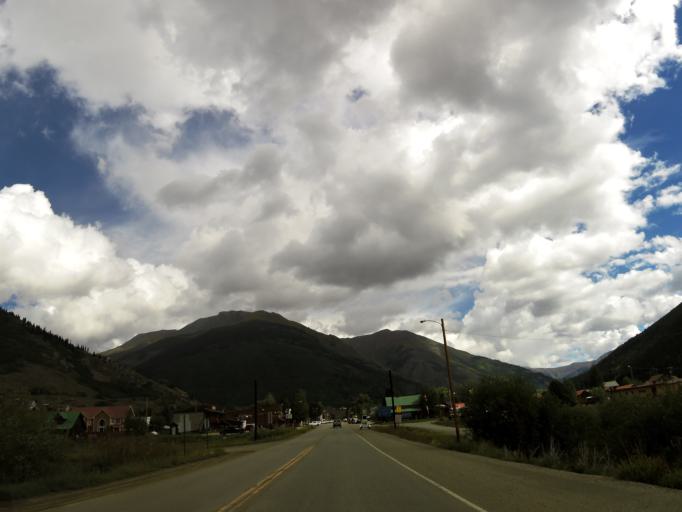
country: US
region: Colorado
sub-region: San Juan County
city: Silverton
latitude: 37.8062
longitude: -107.6694
